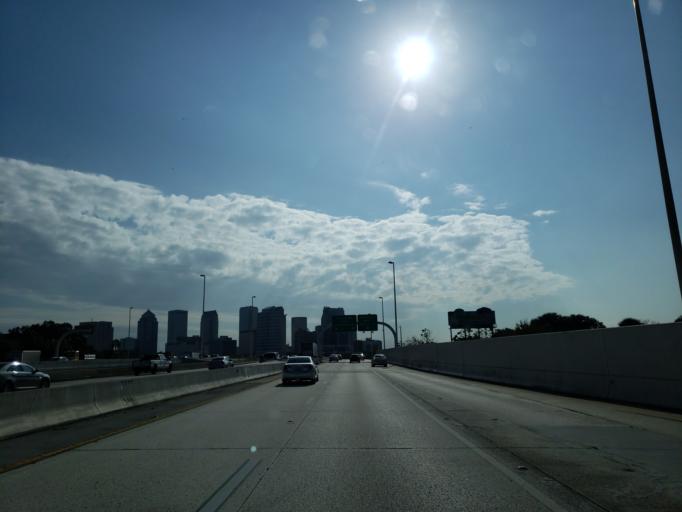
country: US
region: Florida
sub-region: Hillsborough County
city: Tampa
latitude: 27.9611
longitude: -82.4543
